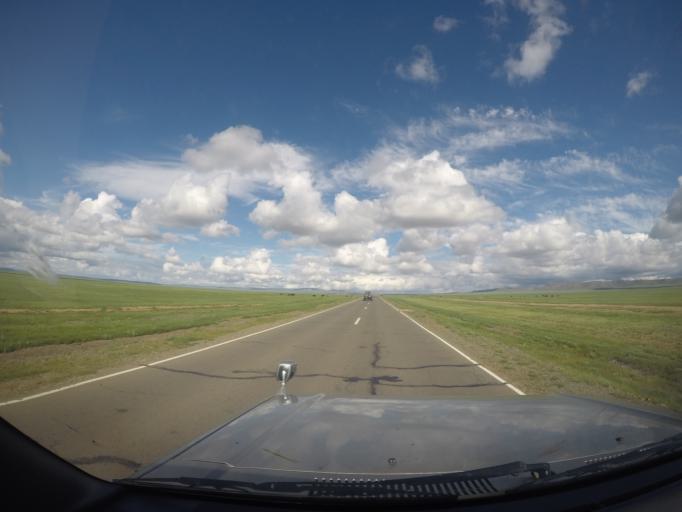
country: MN
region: Hentiy
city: Moron
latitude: 47.4205
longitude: 110.0302
